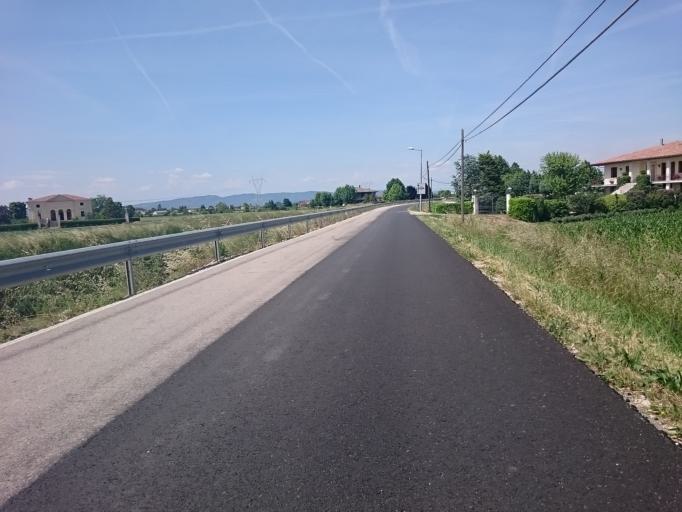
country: IT
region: Veneto
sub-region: Provincia di Padova
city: Lozzo Atestino
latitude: 45.3082
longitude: 11.6026
